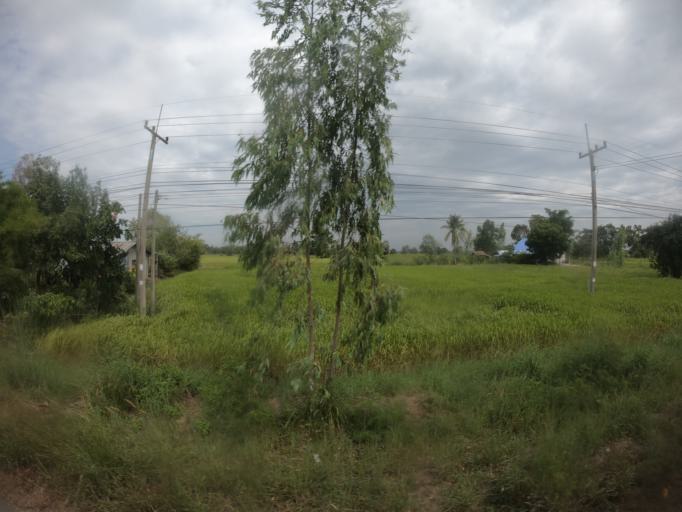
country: TH
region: Maha Sarakham
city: Chiang Yuen
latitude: 16.3382
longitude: 103.1633
